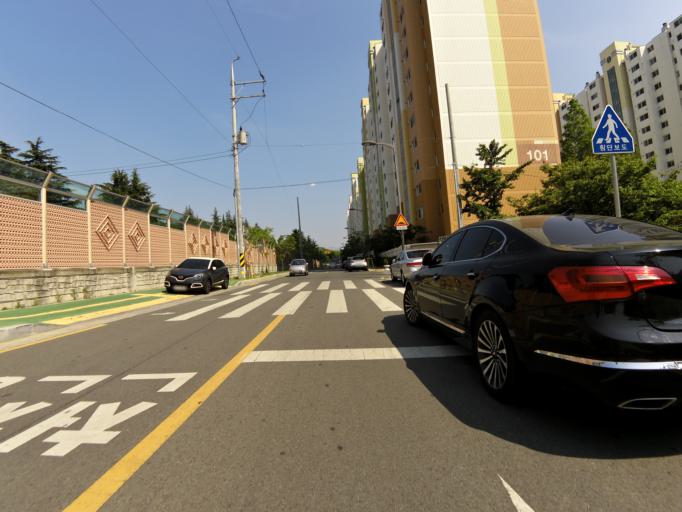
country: KR
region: Daegu
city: Daegu
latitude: 35.8750
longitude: 128.6528
